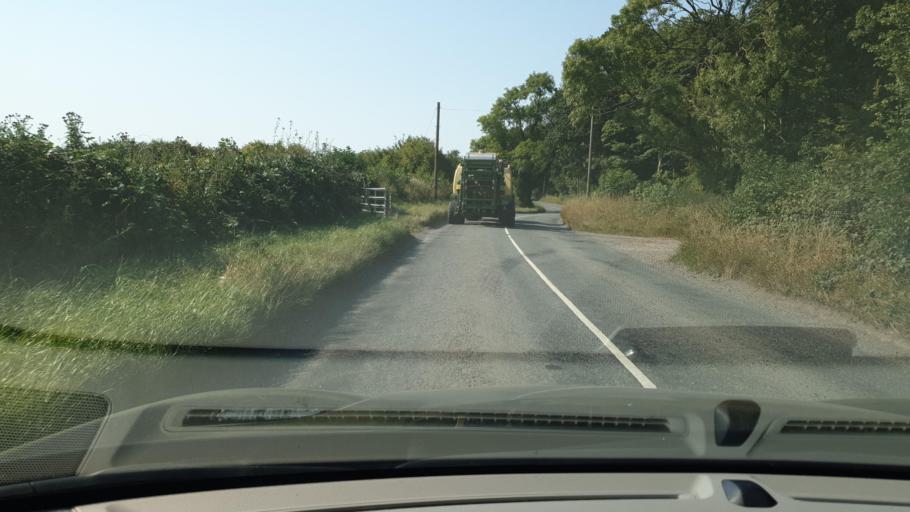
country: IE
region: Leinster
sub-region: An Mhi
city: Athboy
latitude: 53.6138
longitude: -6.8998
